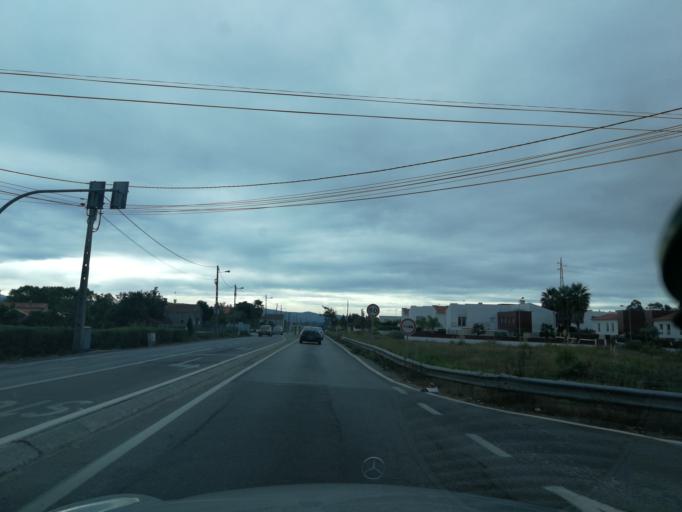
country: PT
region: Aveiro
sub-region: Agueda
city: Agueda
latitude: 40.5909
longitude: -8.4531
